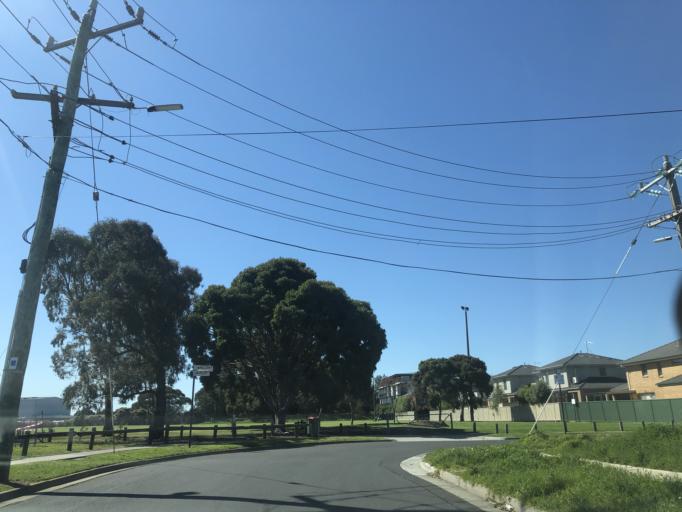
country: AU
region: Victoria
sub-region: Monash
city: Clayton
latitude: -37.9057
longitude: 145.1259
